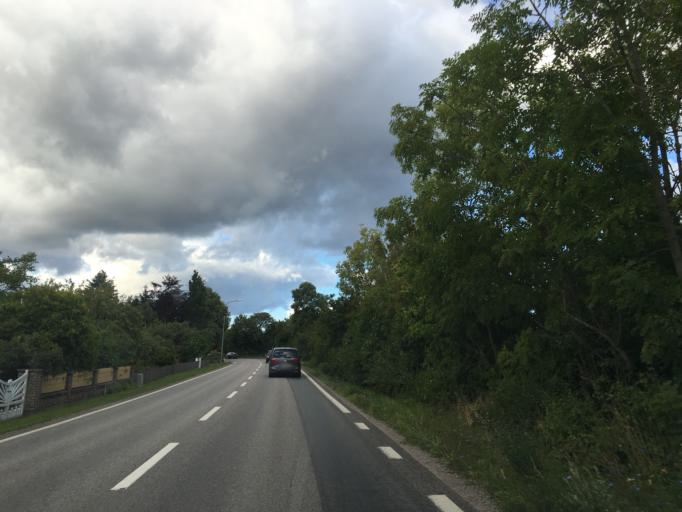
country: SE
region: Kalmar
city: Faerjestaden
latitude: 56.6390
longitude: 16.5165
